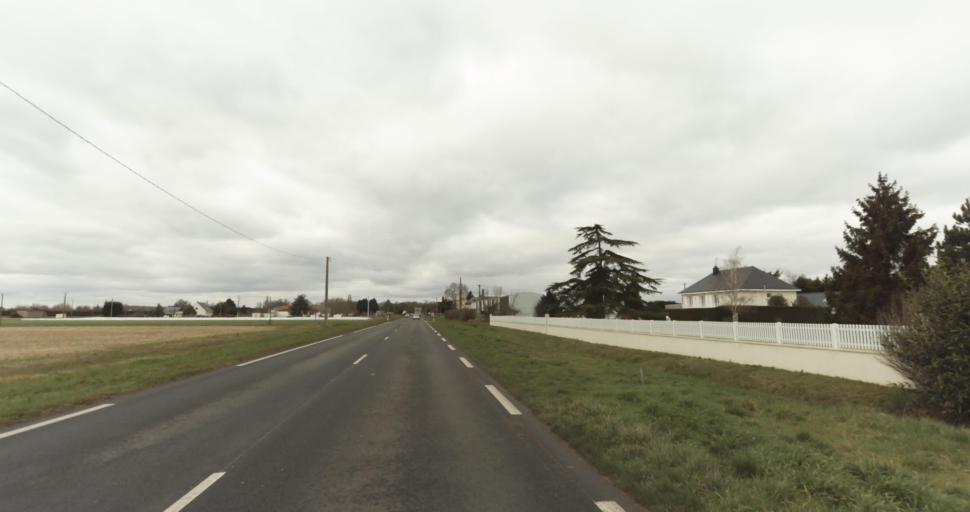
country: FR
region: Pays de la Loire
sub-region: Departement de Maine-et-Loire
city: Allonnes
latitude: 47.2995
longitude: -0.0044
